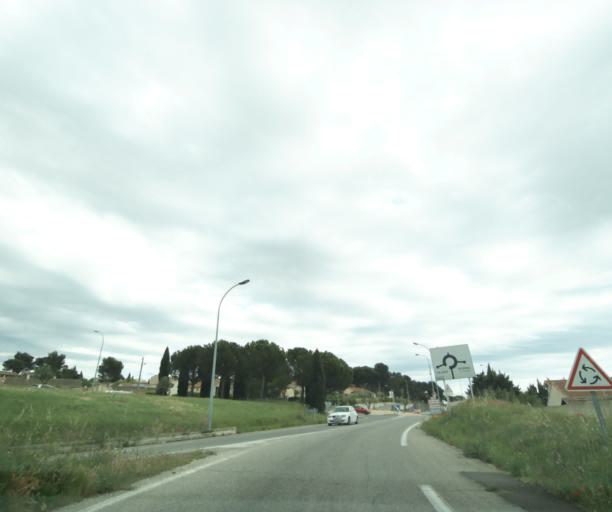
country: FR
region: Provence-Alpes-Cote d'Azur
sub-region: Departement des Bouches-du-Rhone
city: Rognac
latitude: 43.4927
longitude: 5.2331
